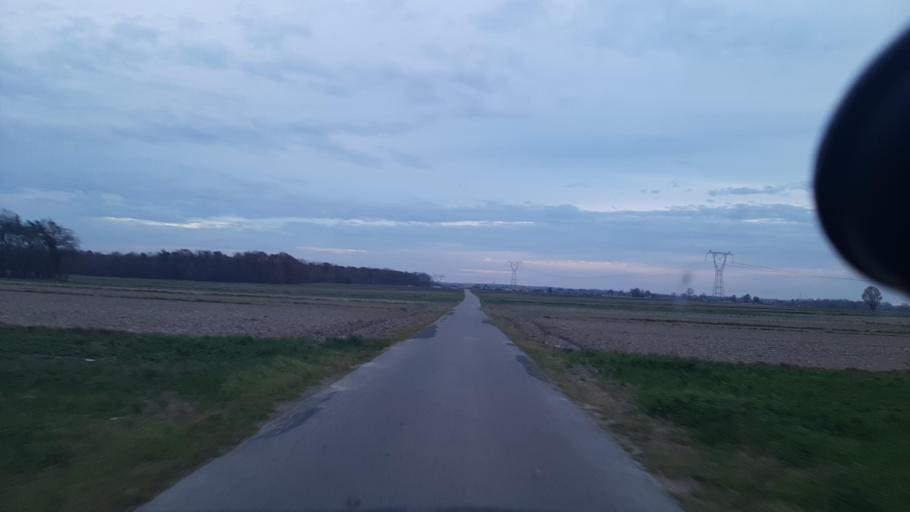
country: PL
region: Lublin Voivodeship
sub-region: Powiat lubelski
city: Garbow
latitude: 51.3755
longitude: 22.3728
